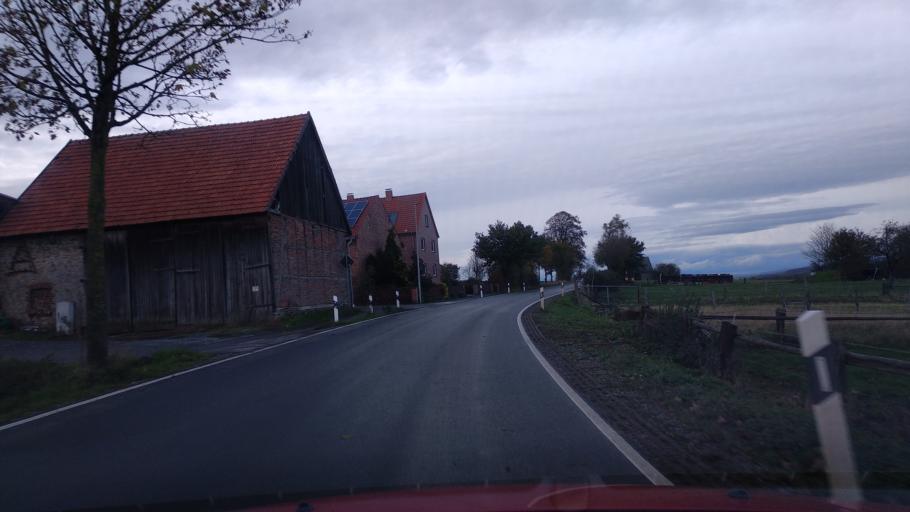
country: DE
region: North Rhine-Westphalia
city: Borgentreich
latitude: 51.6600
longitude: 9.2699
